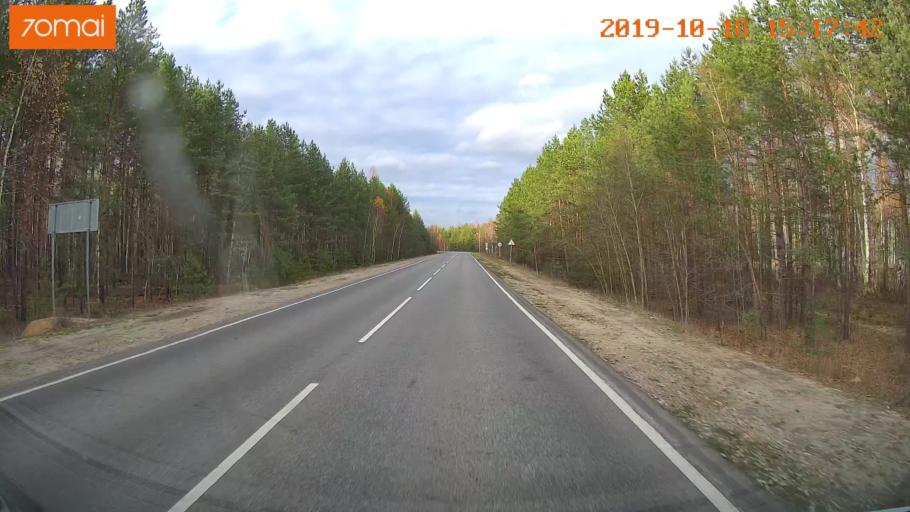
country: RU
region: Vladimir
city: Anopino
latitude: 55.6538
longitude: 40.7272
